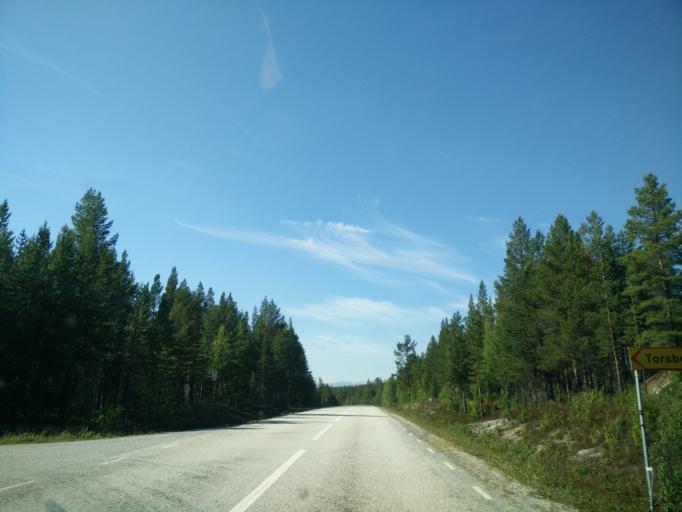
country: SE
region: Jaemtland
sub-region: Are Kommun
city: Jarpen
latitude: 62.8273
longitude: 13.4660
